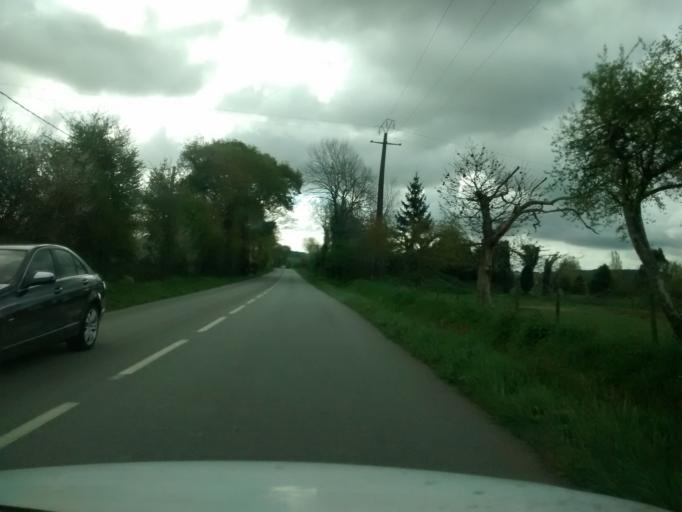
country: FR
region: Brittany
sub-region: Departement du Morbihan
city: Ruffiac
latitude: 47.8165
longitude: -2.2760
